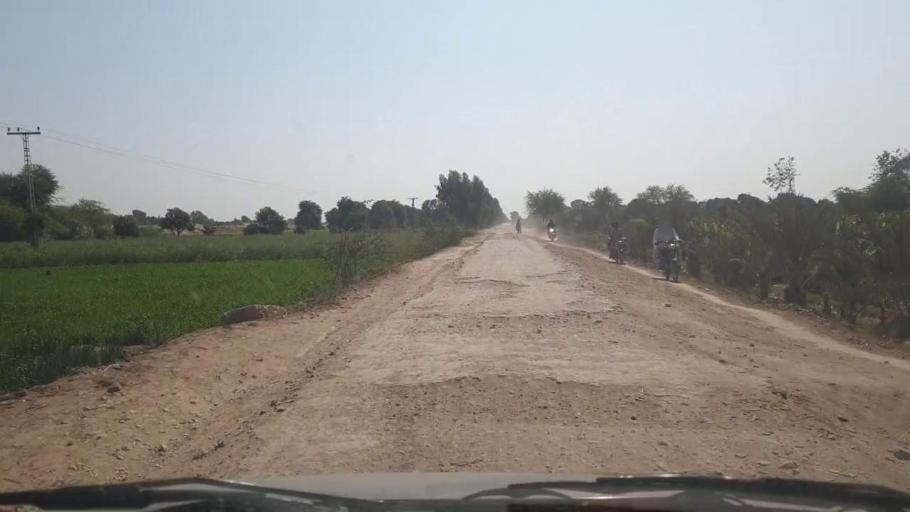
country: PK
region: Sindh
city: Samaro
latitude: 25.2703
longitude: 69.3459
